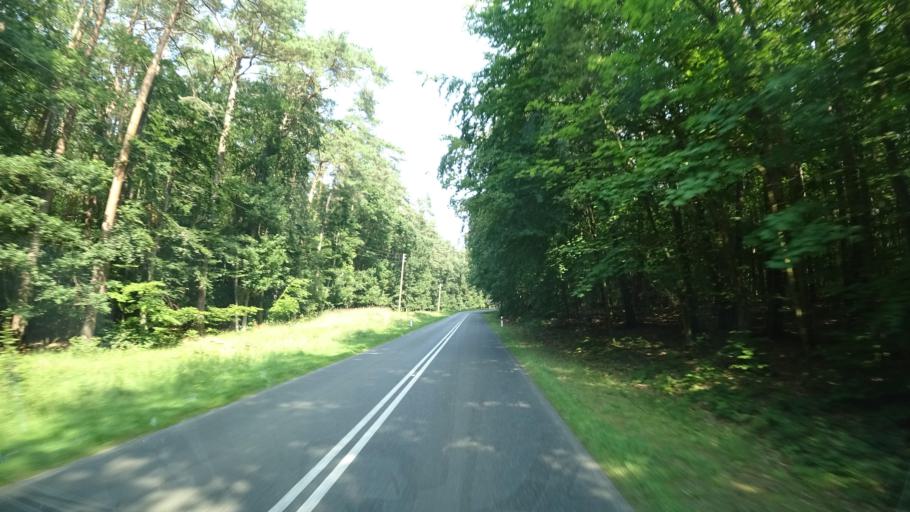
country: PL
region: West Pomeranian Voivodeship
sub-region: Powiat kamienski
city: Miedzyzdroje
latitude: 53.9647
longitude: 14.5534
